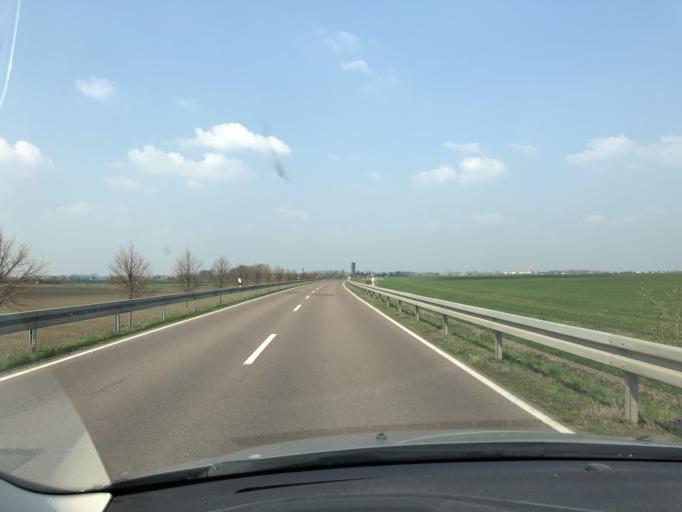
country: DE
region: Saxony-Anhalt
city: Zorbig
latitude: 51.6051
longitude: 12.1289
